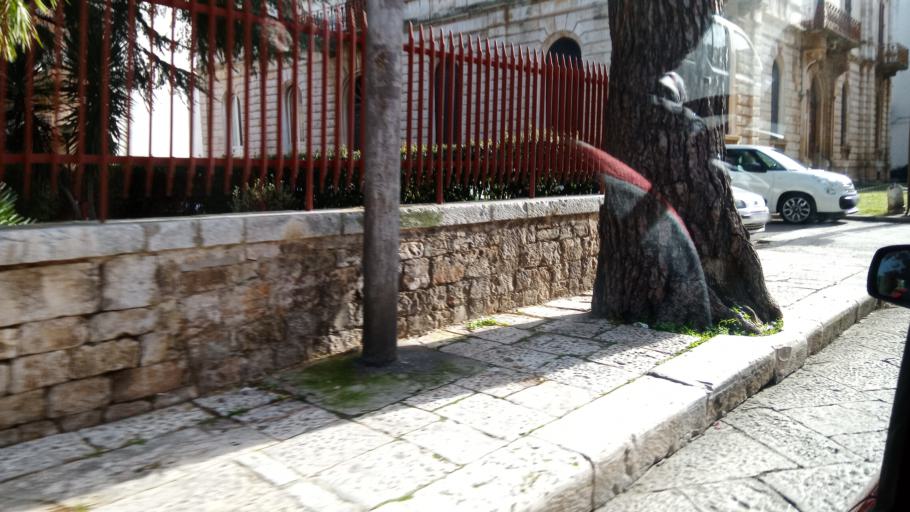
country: IT
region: Apulia
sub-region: Provincia di Bari
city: Castellana
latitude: 40.8867
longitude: 17.1667
